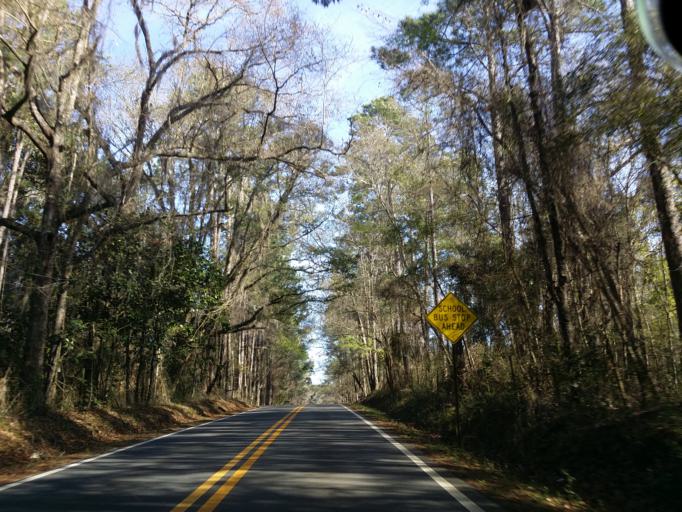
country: US
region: Florida
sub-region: Leon County
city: Woodville
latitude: 30.3900
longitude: -84.1553
